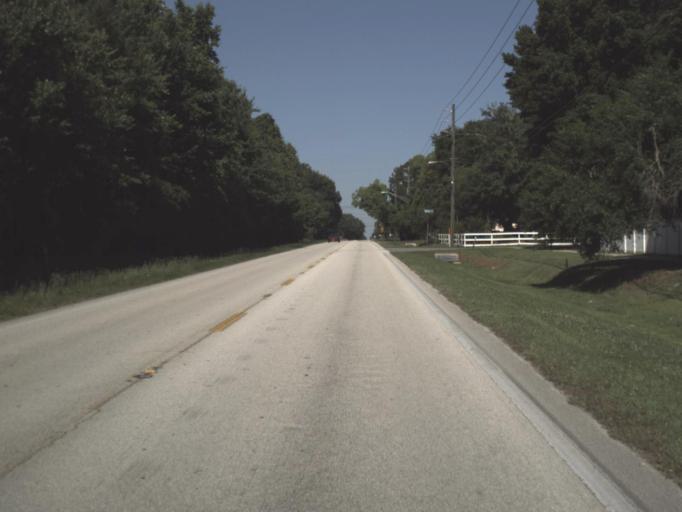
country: US
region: Florida
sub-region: Duval County
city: Baldwin
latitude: 30.3126
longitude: -81.8639
